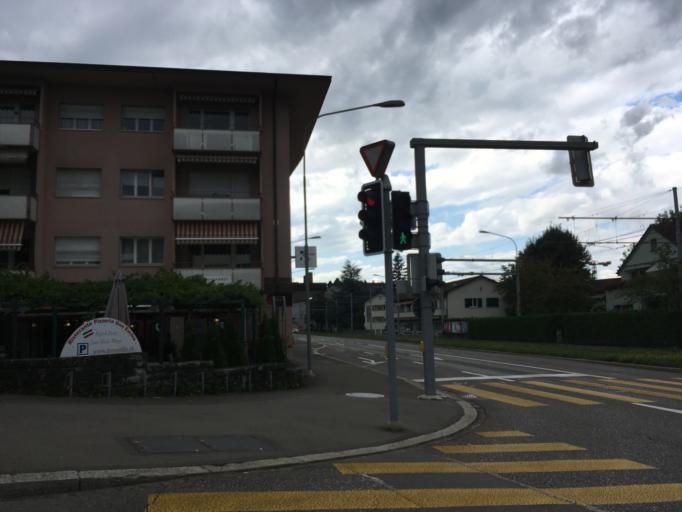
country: CH
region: Zurich
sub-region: Bezirk Zuerich
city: Zuerich (Kreis 12)
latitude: 47.4030
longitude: 8.5766
